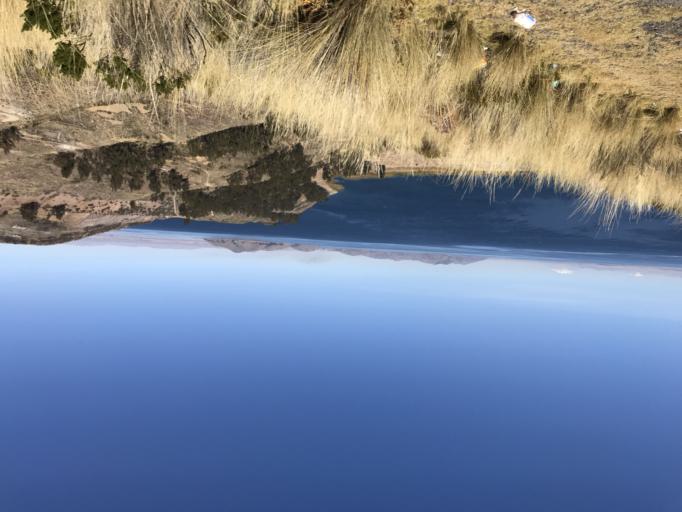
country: BO
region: La Paz
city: San Pablo
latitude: -16.2095
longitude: -68.8370
